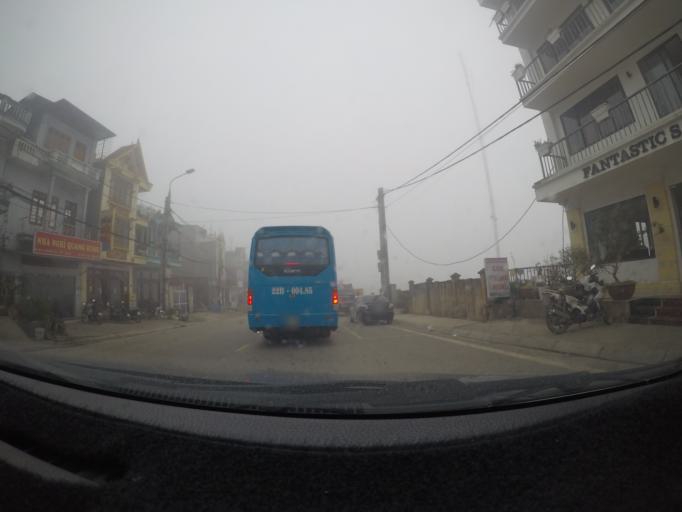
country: VN
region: Lao Cai
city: Sa Pa
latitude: 22.3395
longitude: 103.8438
